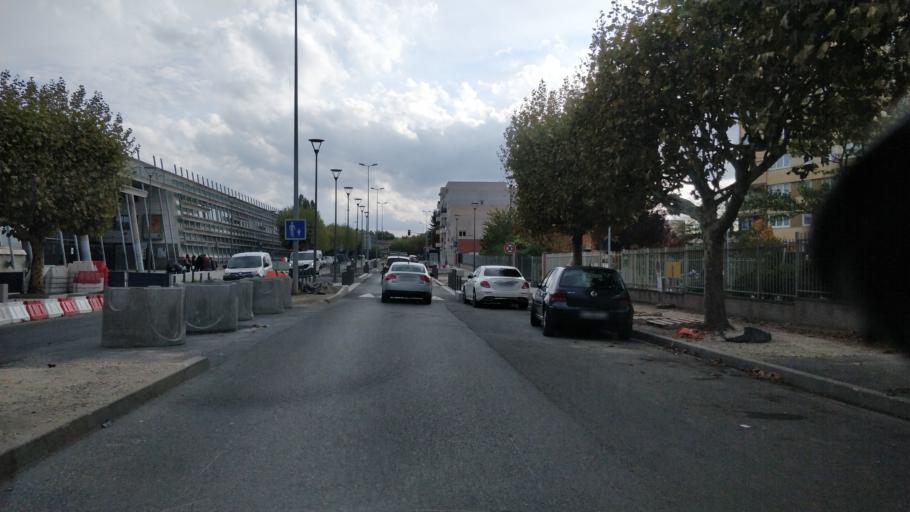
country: FR
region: Ile-de-France
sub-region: Departement de Seine-Saint-Denis
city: Clichy-sous-Bois
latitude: 48.9032
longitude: 2.5477
